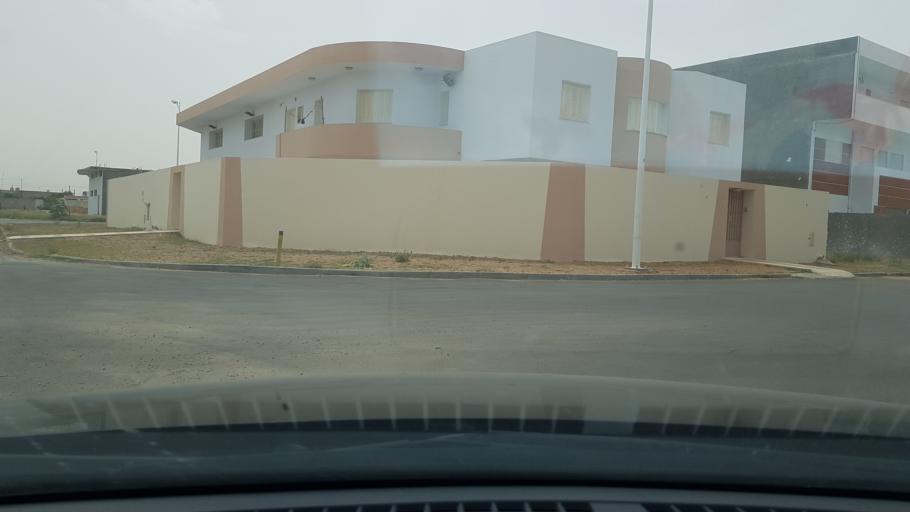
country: TN
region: Safaqis
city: Al Qarmadah
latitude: 34.8254
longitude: 10.7420
